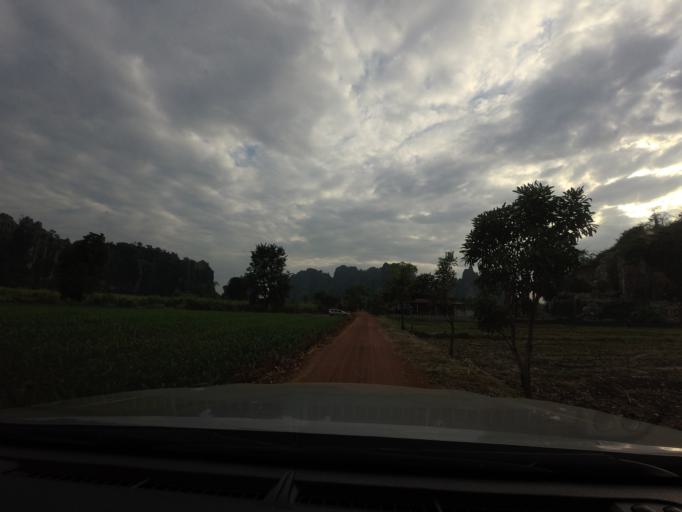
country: TH
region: Phitsanulok
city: Noen Maprang
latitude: 16.5821
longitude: 100.6852
